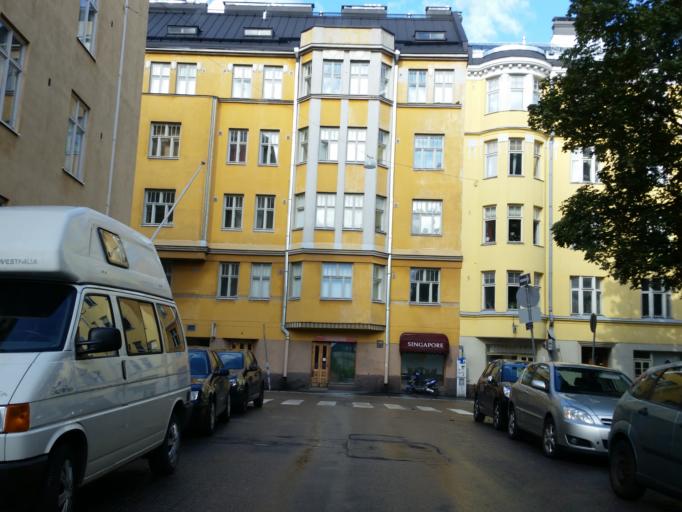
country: FI
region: Uusimaa
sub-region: Helsinki
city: Helsinki
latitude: 60.1670
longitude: 24.9243
